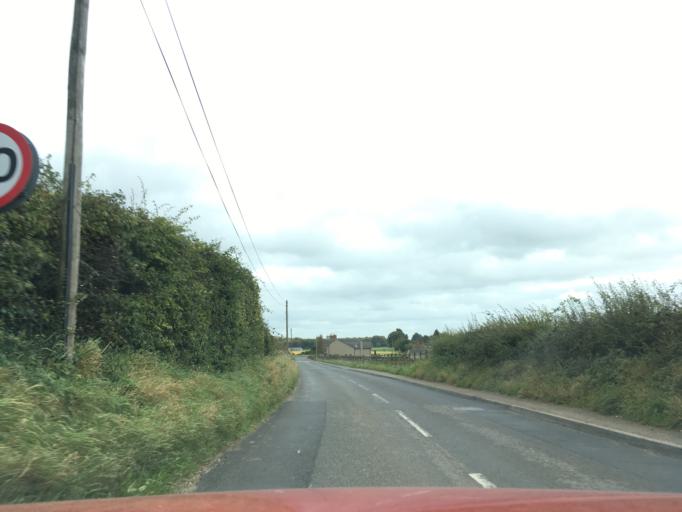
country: GB
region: England
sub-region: South Gloucestershire
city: Horton
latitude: 51.5787
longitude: -2.3155
